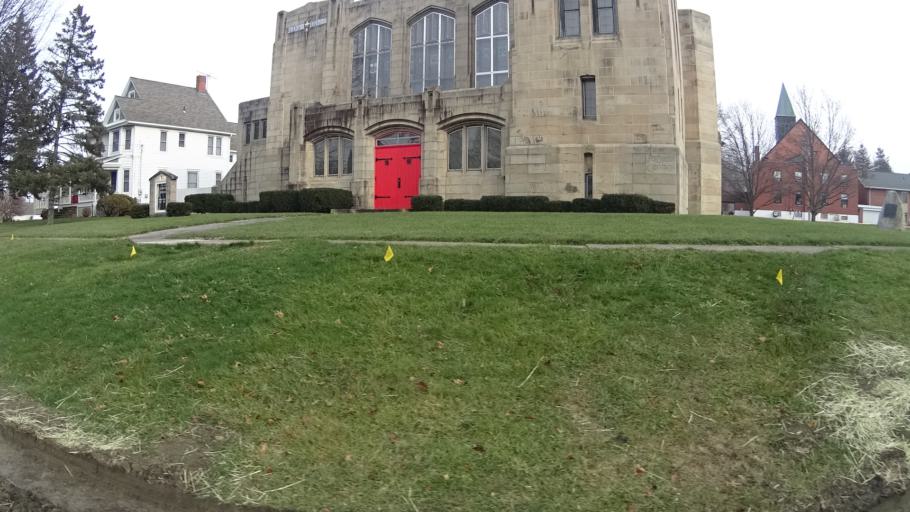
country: US
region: Ohio
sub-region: Lorain County
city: Amherst
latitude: 41.3944
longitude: -82.2270
